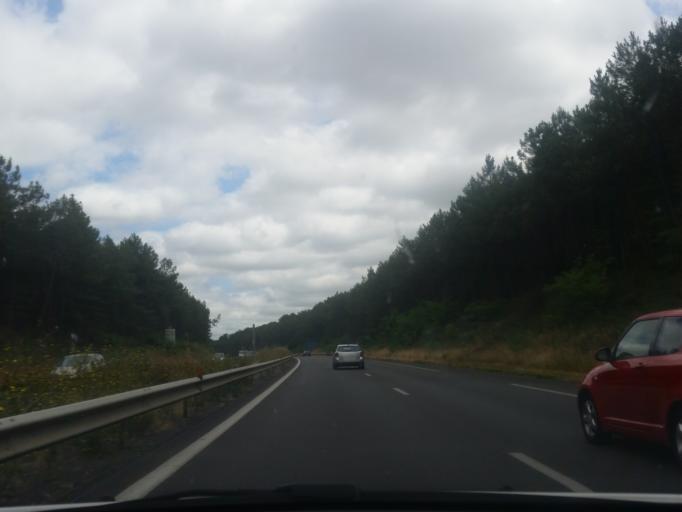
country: FR
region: Pays de la Loire
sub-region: Departement de Maine-et-Loire
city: Baune
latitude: 47.5223
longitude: -0.3567
